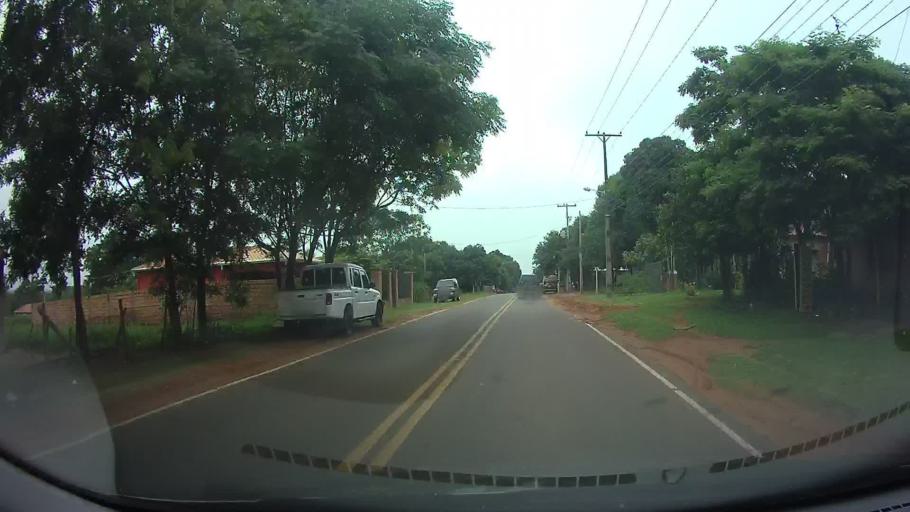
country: PY
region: Central
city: Itaugua
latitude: -25.3733
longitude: -57.3482
